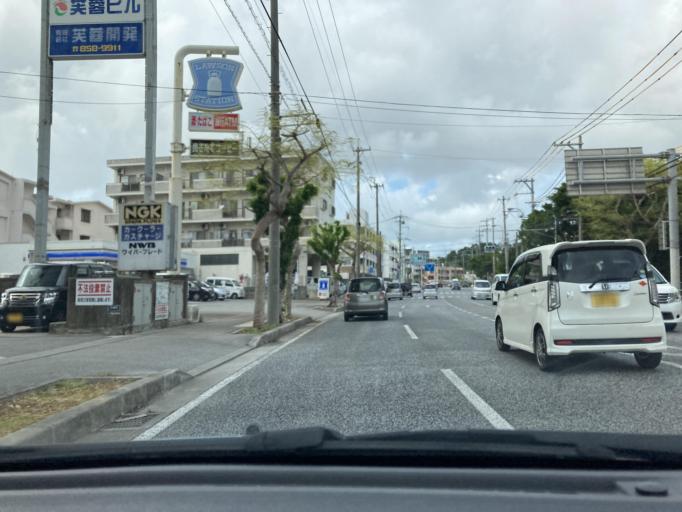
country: JP
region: Okinawa
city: Tomigusuku
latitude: 26.1792
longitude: 127.6811
